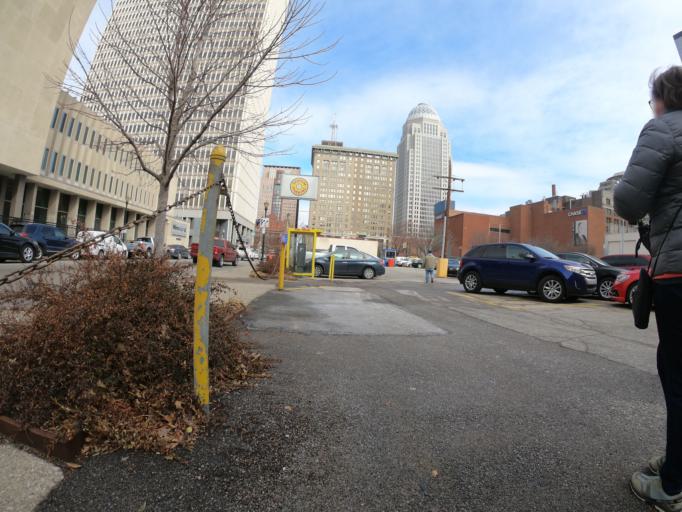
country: US
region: Kentucky
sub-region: Jefferson County
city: Louisville
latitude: 38.2527
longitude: -85.7588
